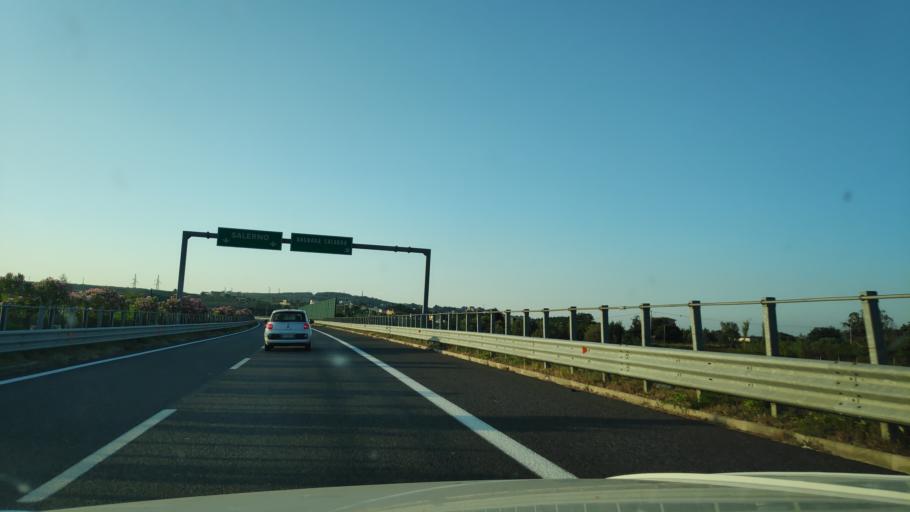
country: IT
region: Calabria
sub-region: Provincia di Reggio Calabria
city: Ceramida-Pellegrina
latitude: 38.3078
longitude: 15.8443
